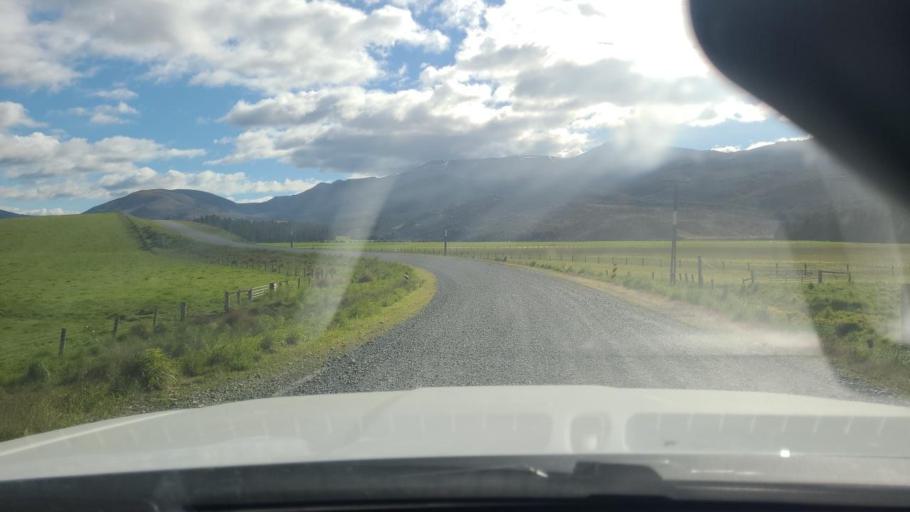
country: NZ
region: Southland
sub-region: Southland District
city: Te Anau
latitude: -45.4807
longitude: 168.1019
